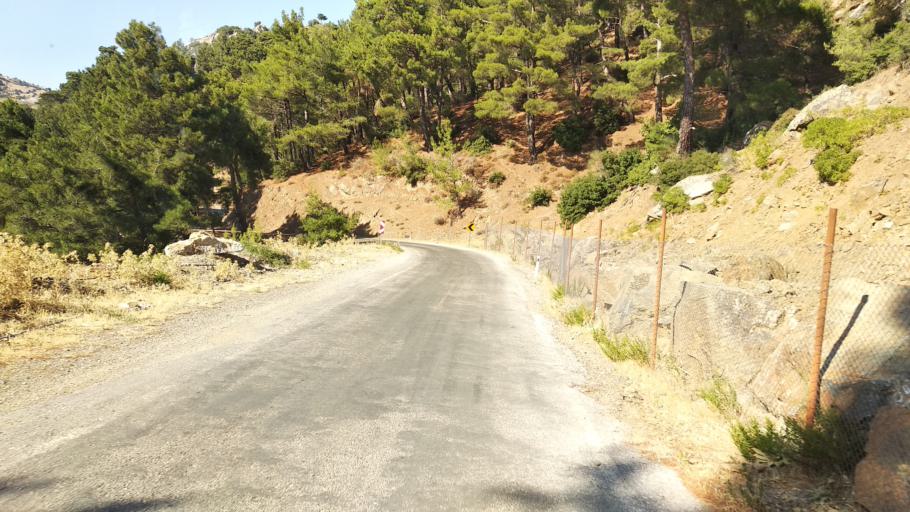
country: TR
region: Izmir
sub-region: Seferihisar
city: Seferhisar
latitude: 38.3170
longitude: 26.9578
